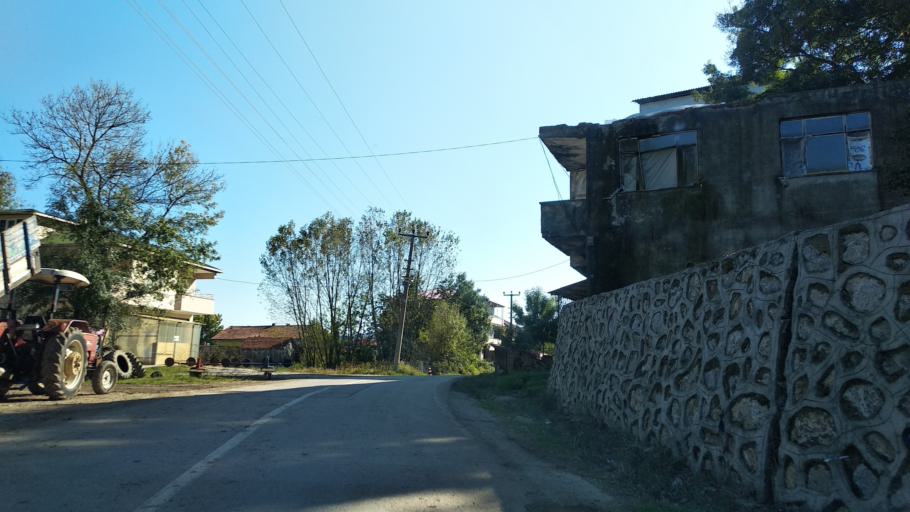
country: TR
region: Sakarya
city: Ortakoy
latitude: 41.0311
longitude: 30.5954
